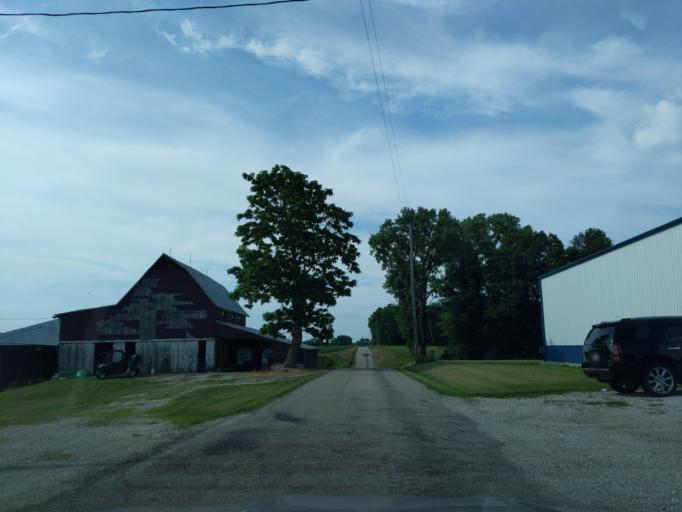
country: US
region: Indiana
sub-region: Ripley County
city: Osgood
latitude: 39.1950
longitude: -85.3893
